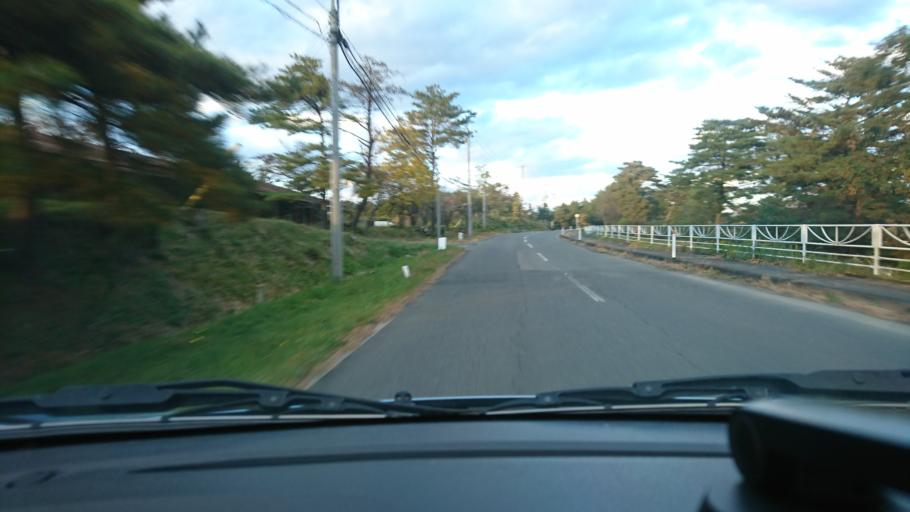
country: JP
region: Iwate
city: Ichinoseki
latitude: 38.8059
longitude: 141.1926
